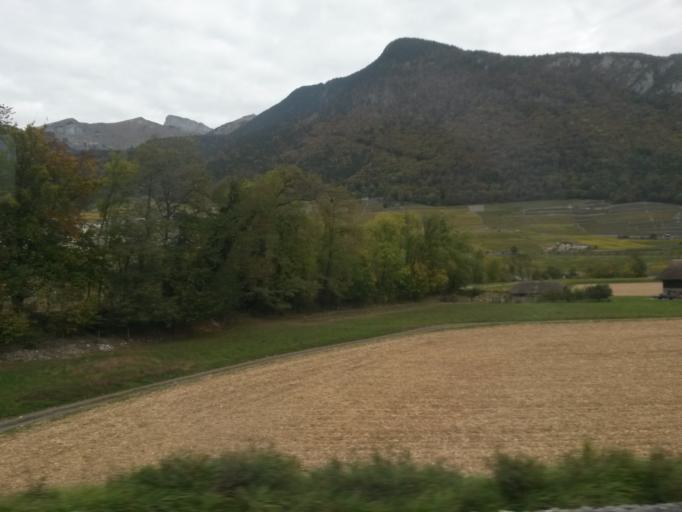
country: CH
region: Vaud
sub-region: Aigle District
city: Aigle
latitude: 46.3248
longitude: 6.9564
